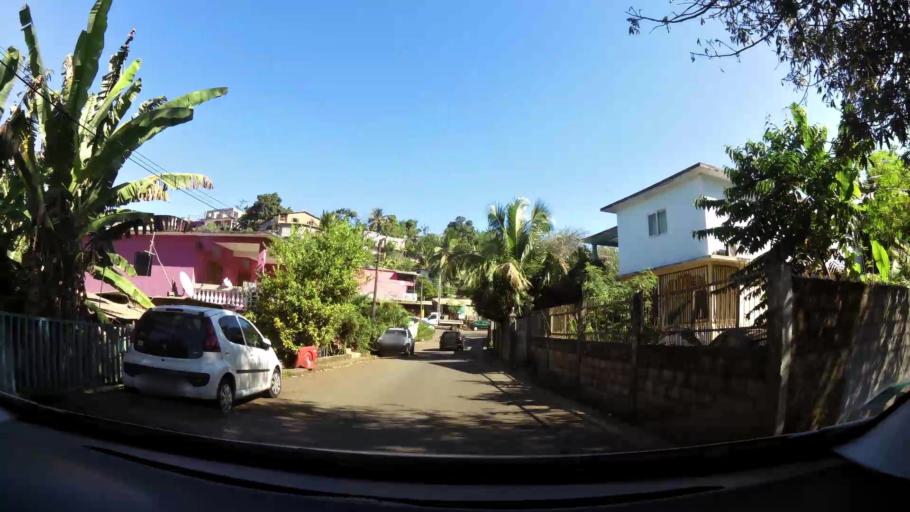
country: YT
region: Mamoudzou
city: Mamoudzou
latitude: -12.7880
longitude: 45.2186
